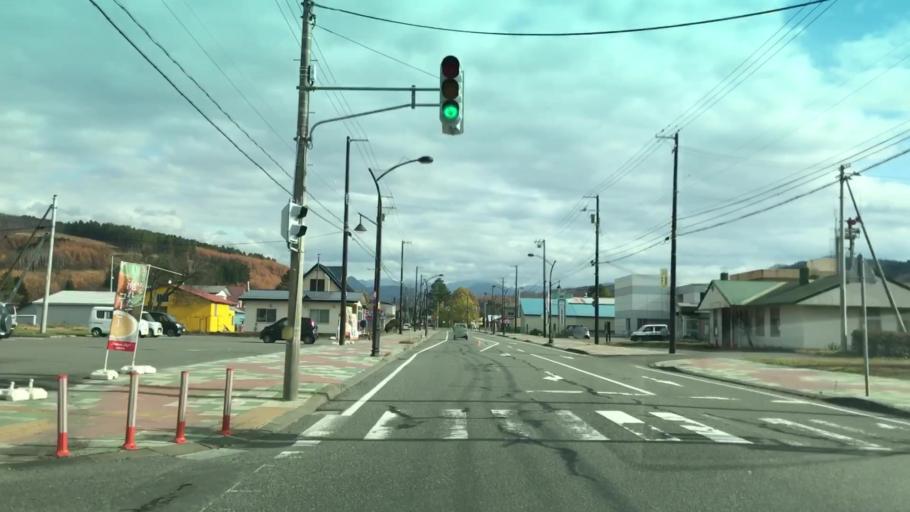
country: JP
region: Hokkaido
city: Shizunai-furukawacho
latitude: 42.7264
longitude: 142.3005
